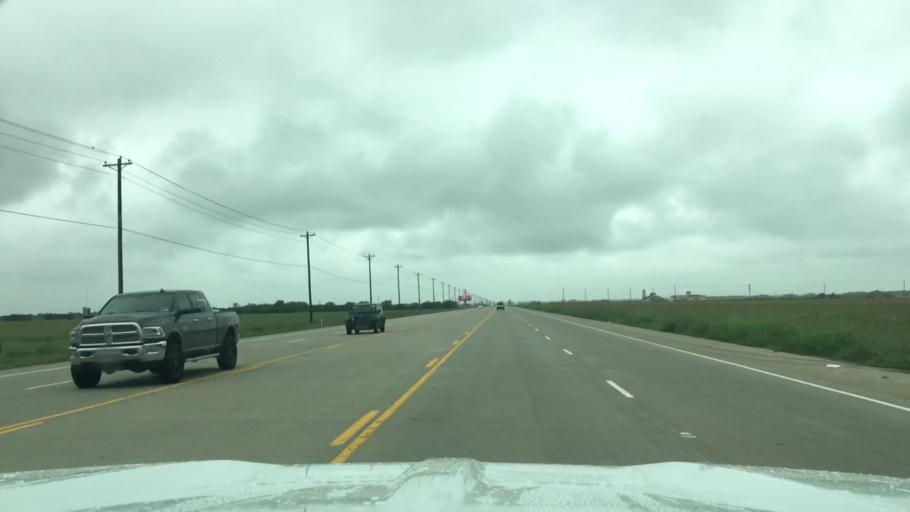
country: US
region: Texas
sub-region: Collin County
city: Prosper
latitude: 33.2190
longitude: -96.8532
